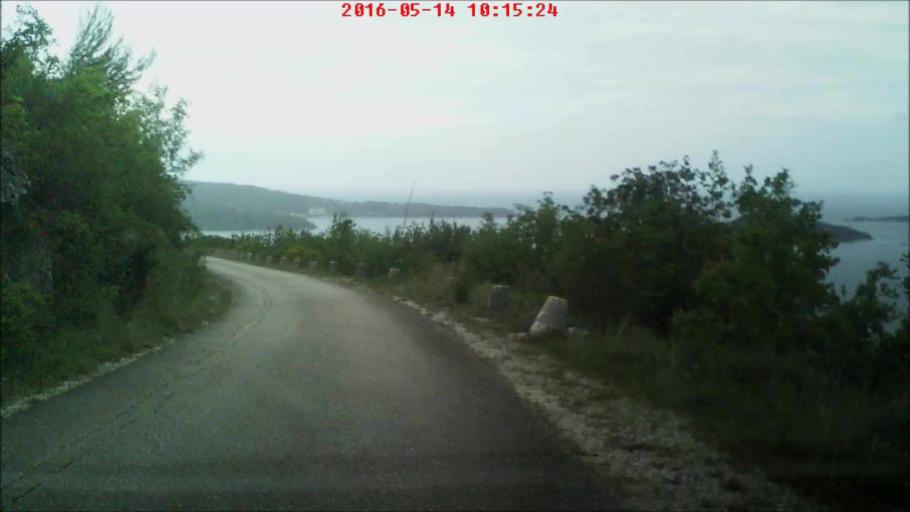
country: HR
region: Dubrovacko-Neretvanska
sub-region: Grad Dubrovnik
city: Mokosica
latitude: 42.7306
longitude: 17.9636
